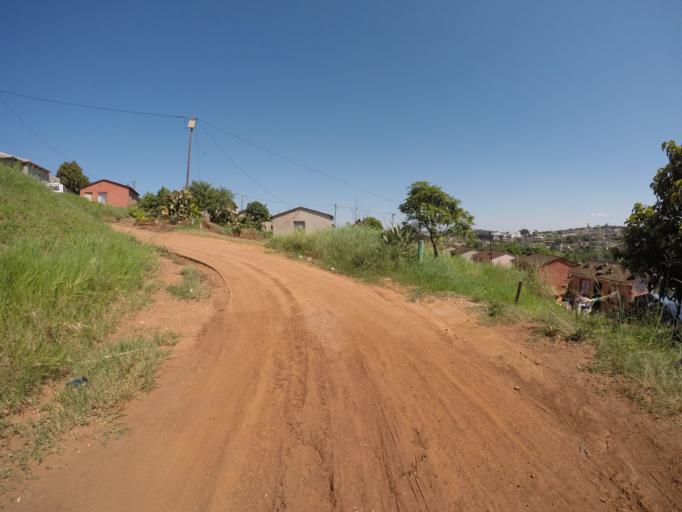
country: ZA
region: KwaZulu-Natal
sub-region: uThungulu District Municipality
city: Empangeni
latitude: -28.7708
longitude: 31.8758
